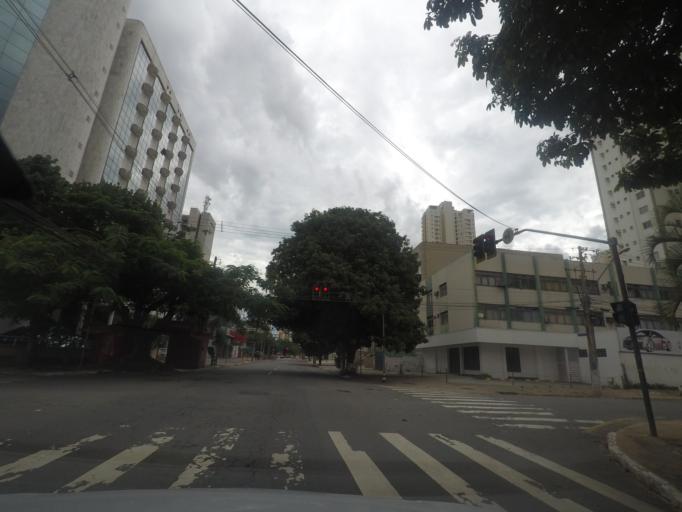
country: BR
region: Goias
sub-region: Goiania
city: Goiania
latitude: -16.6786
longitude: -49.2664
